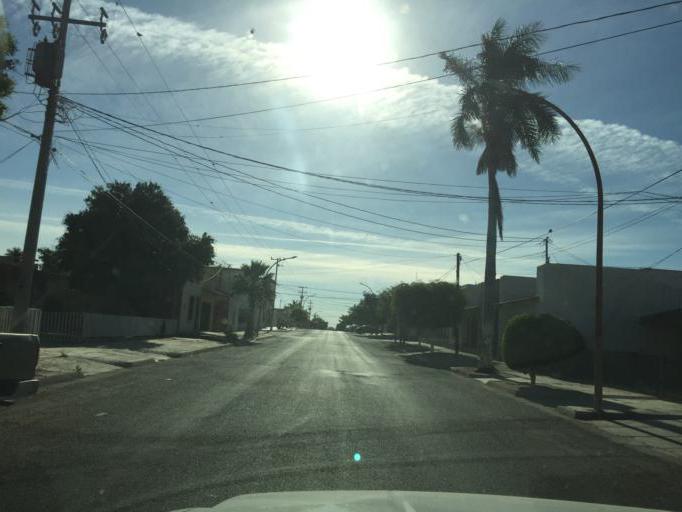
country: MX
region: Sonora
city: Navojoa
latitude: 27.0831
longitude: -109.4506
